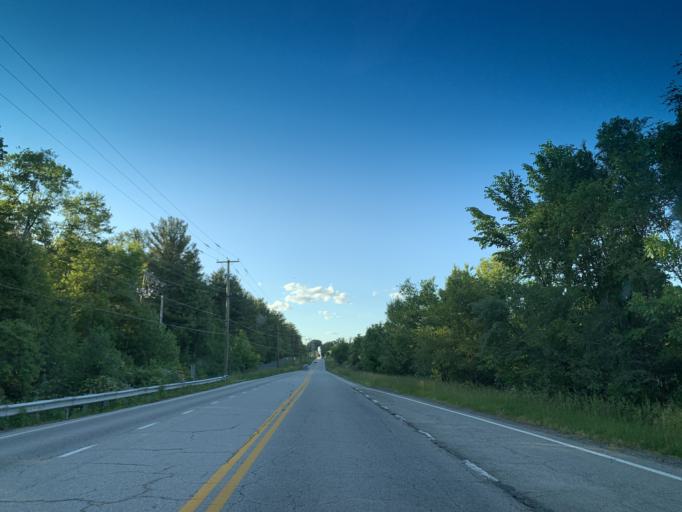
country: US
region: Maryland
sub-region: Cecil County
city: Elkton
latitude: 39.6499
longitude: -75.8130
